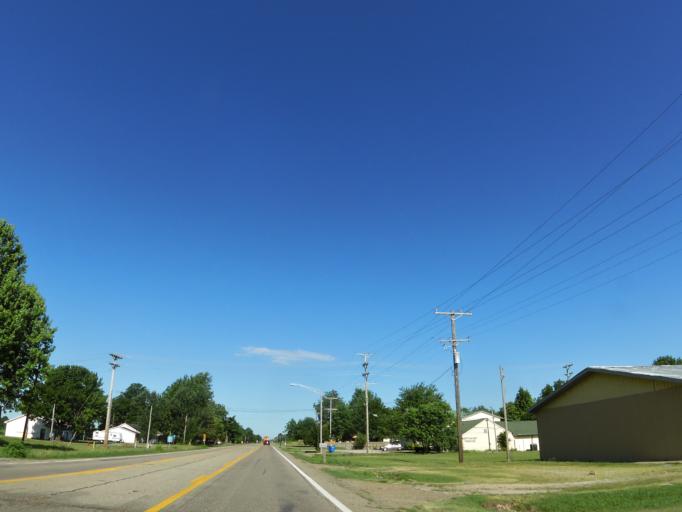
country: US
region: Arkansas
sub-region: Clay County
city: Corning
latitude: 36.4115
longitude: -90.6025
